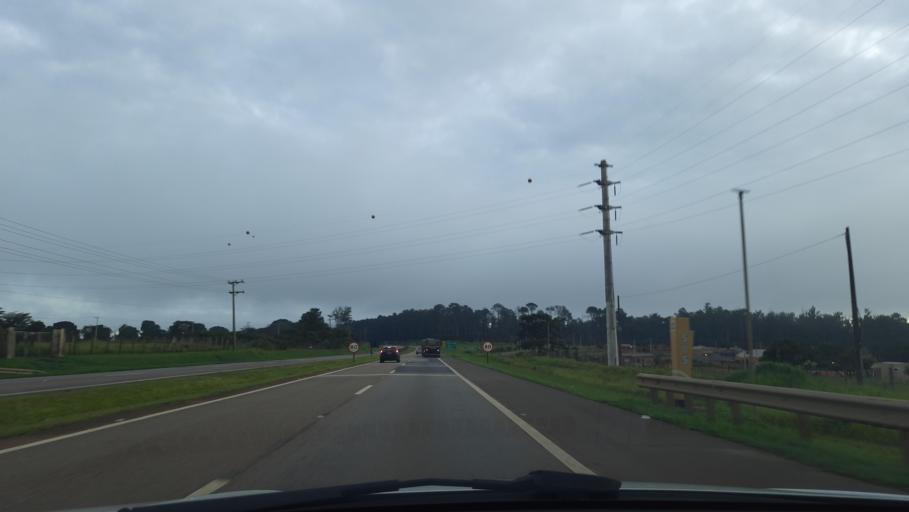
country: BR
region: Sao Paulo
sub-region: Casa Branca
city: Casa Branca
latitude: -21.7611
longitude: -47.0703
